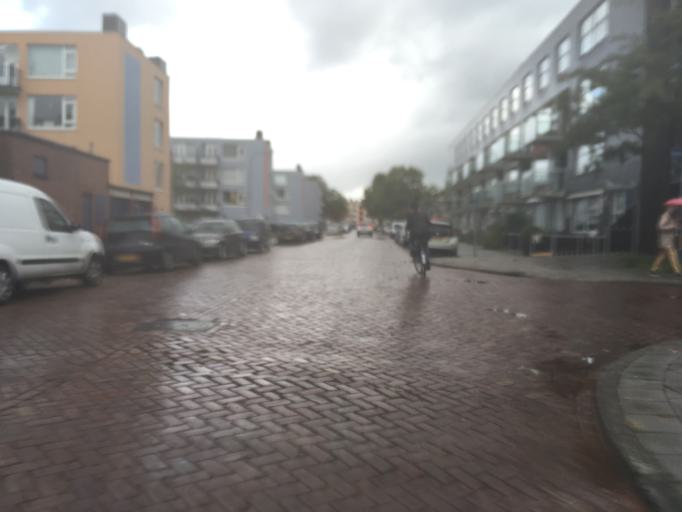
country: NL
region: North Holland
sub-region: Gemeente Haarlem
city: Haarlem
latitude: 52.3761
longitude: 4.6624
